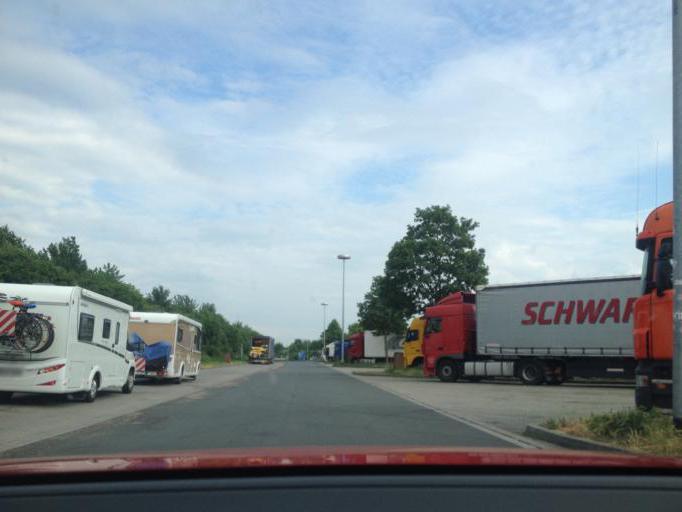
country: DE
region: Saxony-Anhalt
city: Konnern
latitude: 51.6558
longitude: 11.8191
